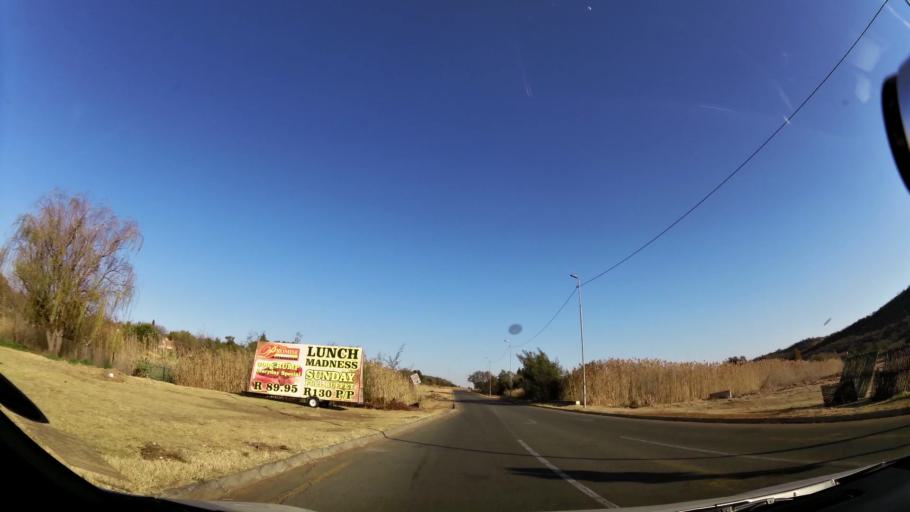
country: ZA
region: Gauteng
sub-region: City of Johannesburg Metropolitan Municipality
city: Johannesburg
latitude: -26.2924
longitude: 28.0727
